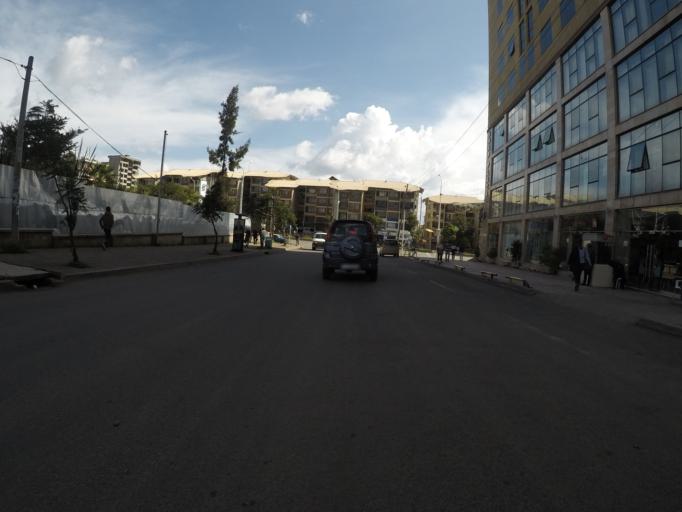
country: ET
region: Adis Abeba
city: Addis Ababa
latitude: 8.9901
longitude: 38.7879
